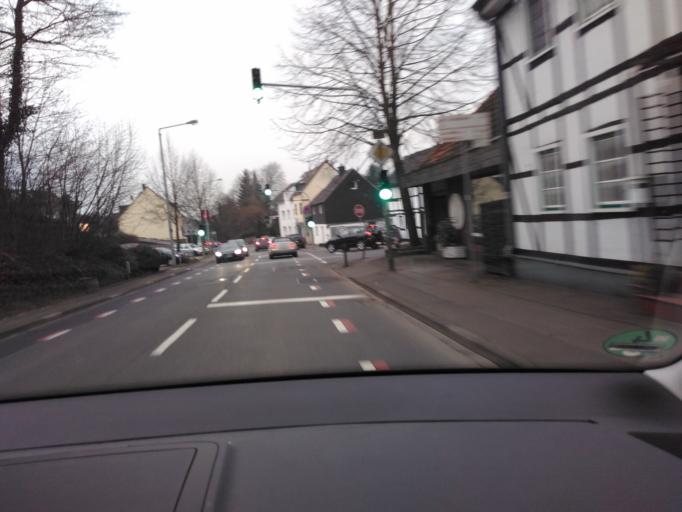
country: DE
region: North Rhine-Westphalia
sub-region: Regierungsbezirk Koln
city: Odenthal
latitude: 51.0453
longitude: 7.0797
